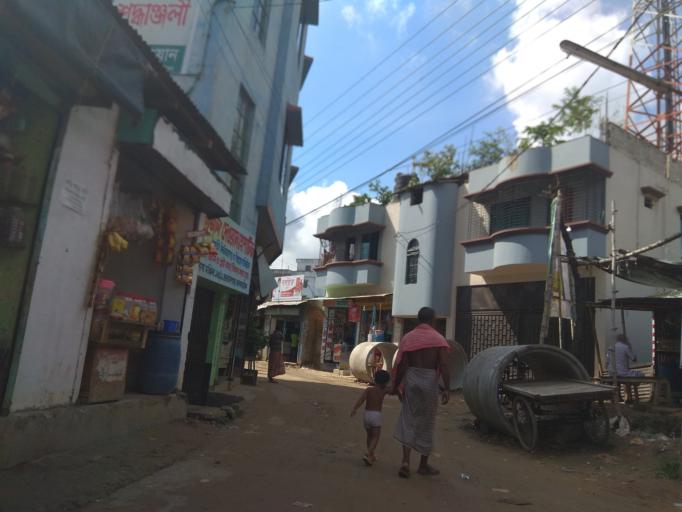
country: BD
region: Dhaka
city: Tungi
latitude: 23.8161
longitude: 90.3867
